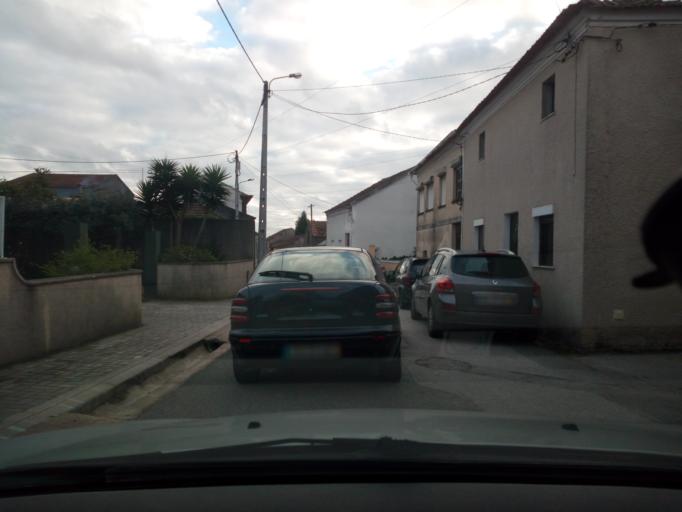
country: PT
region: Aveiro
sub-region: Oliveira do Bairro
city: Oliveira do Bairro
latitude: 40.5475
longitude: -8.4892
